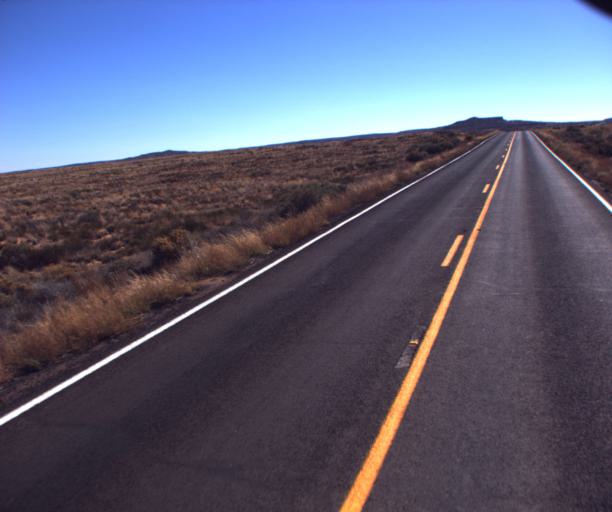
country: US
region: Arizona
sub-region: Navajo County
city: First Mesa
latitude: 35.9787
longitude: -110.7025
